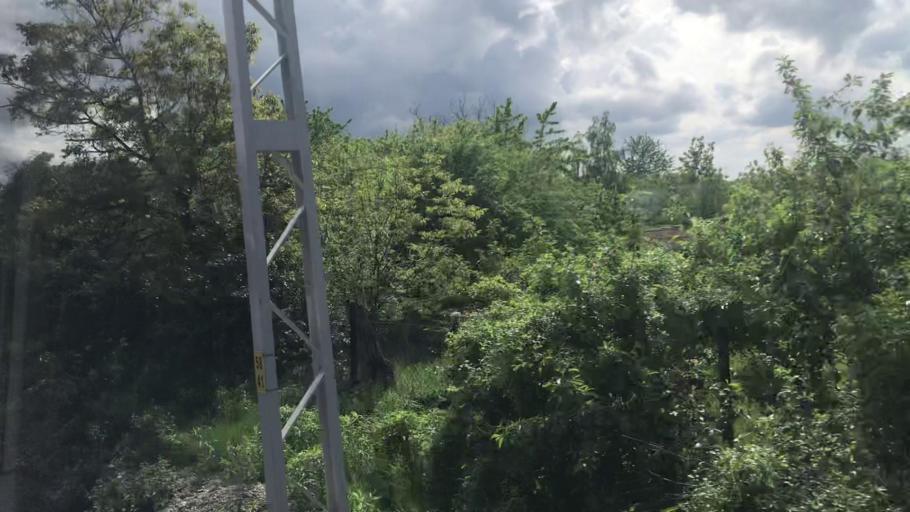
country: PL
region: Lower Silesian Voivodeship
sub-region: Powiat swidnicki
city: Swiebodzice
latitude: 50.8573
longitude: 16.3441
